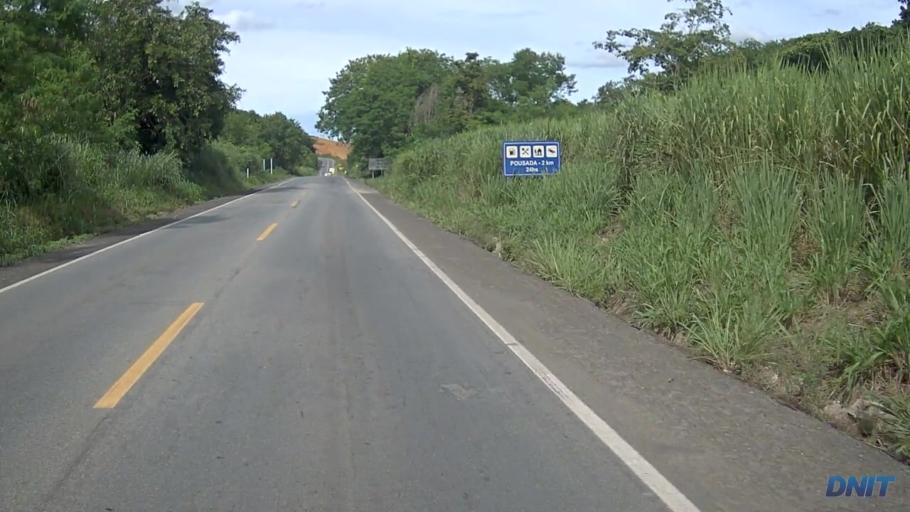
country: BR
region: Minas Gerais
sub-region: Ipaba
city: Ipaba
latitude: -19.2963
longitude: -42.3633
